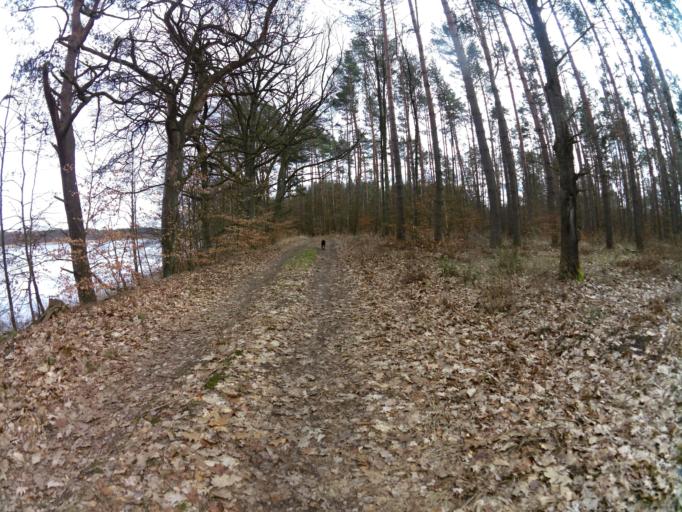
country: PL
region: Lubusz
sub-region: Powiat gorzowski
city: Lubiszyn
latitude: 52.7888
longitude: 14.8377
